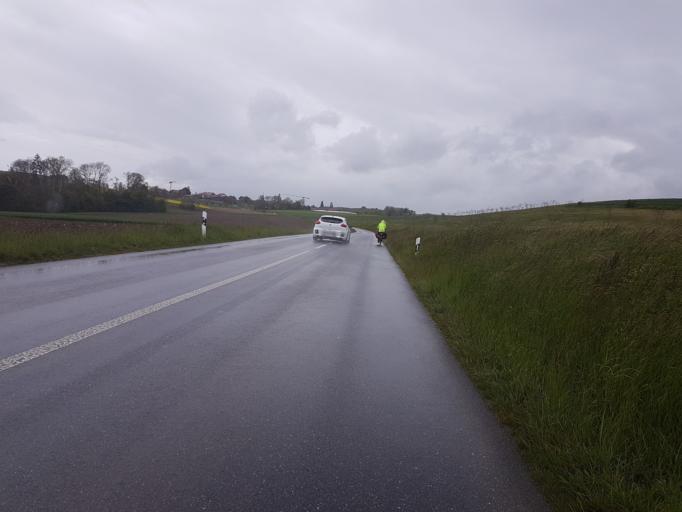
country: CH
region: Vaud
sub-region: Gros-de-Vaud District
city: Penthalaz
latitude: 46.5909
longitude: 6.5217
